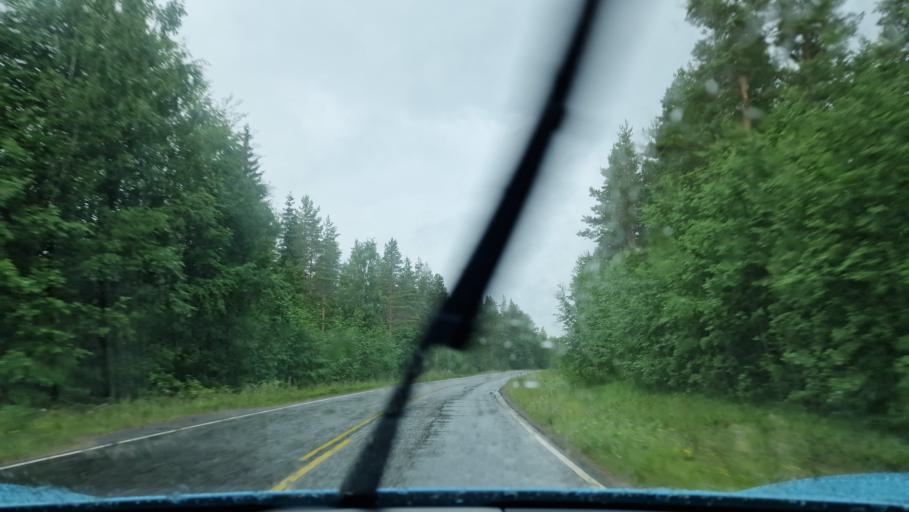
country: FI
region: Southern Ostrobothnia
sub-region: Jaerviseutu
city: Soini
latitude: 62.8183
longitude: 24.3513
